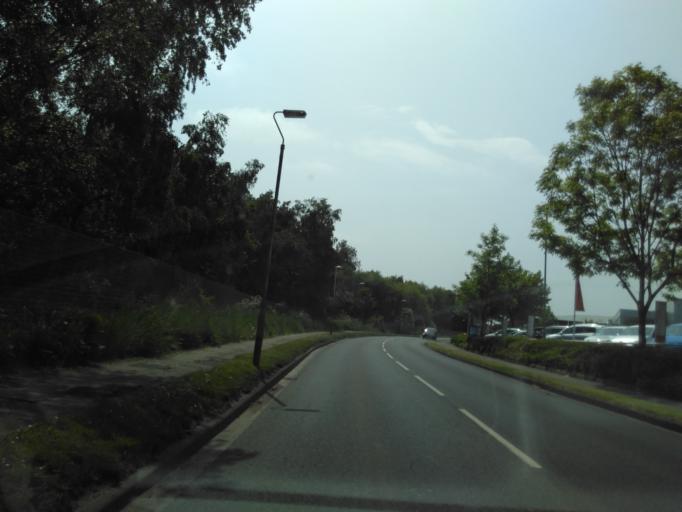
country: GB
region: England
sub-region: Kent
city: Canterbury
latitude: 51.2951
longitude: 1.0955
